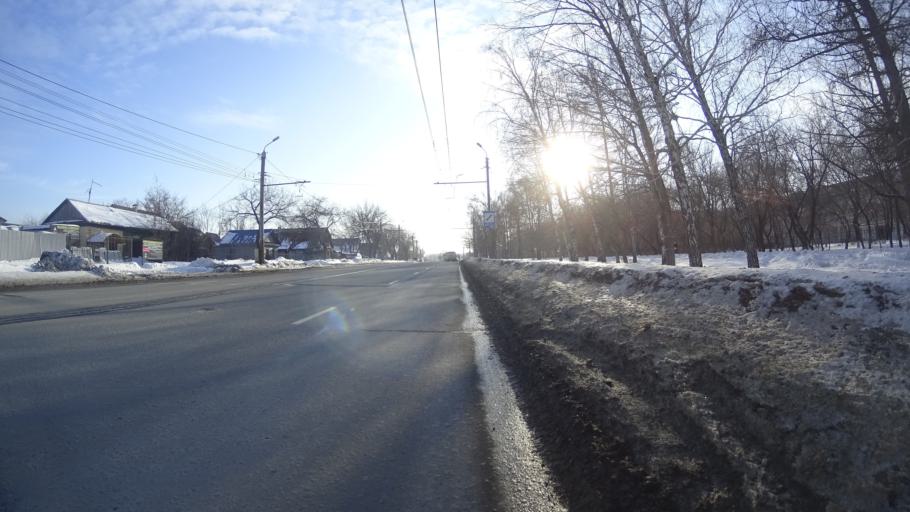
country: RU
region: Chelyabinsk
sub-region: Gorod Chelyabinsk
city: Chelyabinsk
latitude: 55.1857
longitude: 61.4599
